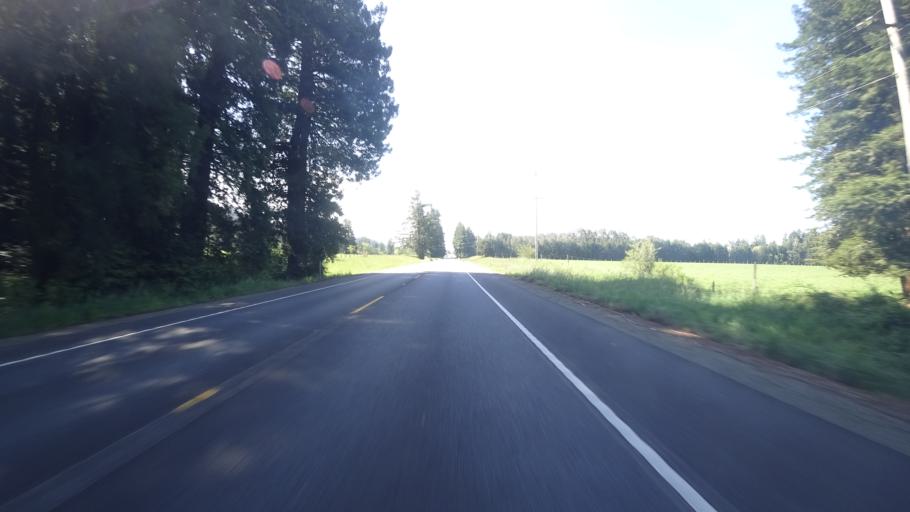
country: US
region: California
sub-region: Del Norte County
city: Bertsch-Oceanview
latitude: 41.9078
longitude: -124.1366
